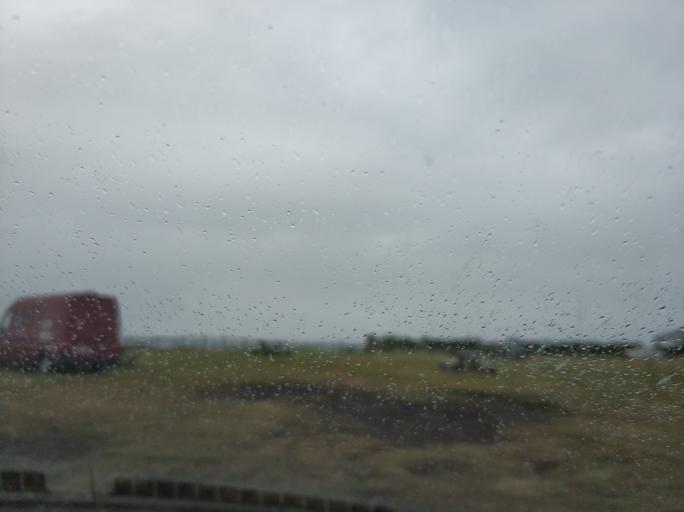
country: ES
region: Asturias
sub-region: Province of Asturias
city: Tineo
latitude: 43.5675
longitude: -6.4703
